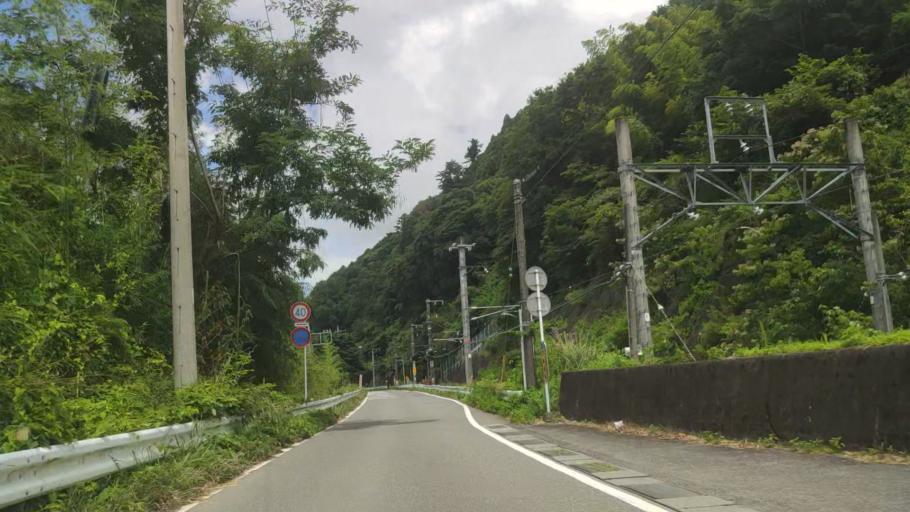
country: JP
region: Shizuoka
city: Fujinomiya
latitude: 35.2454
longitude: 138.4931
